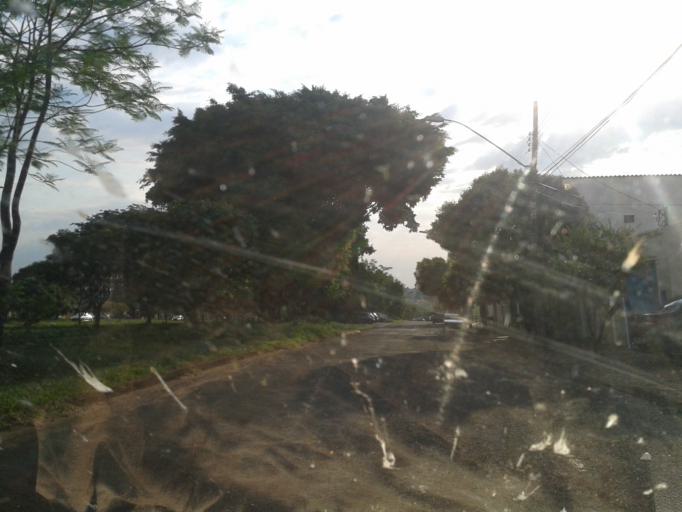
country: BR
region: Minas Gerais
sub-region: Uberlandia
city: Uberlandia
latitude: -18.9413
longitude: -48.3171
